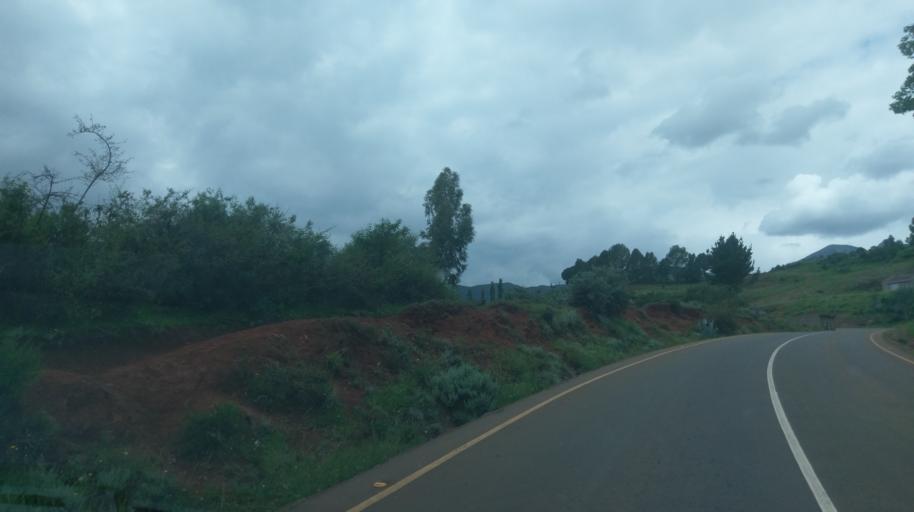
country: LS
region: Butha-Buthe
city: Butha-Buthe
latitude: -29.0359
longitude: 28.2818
